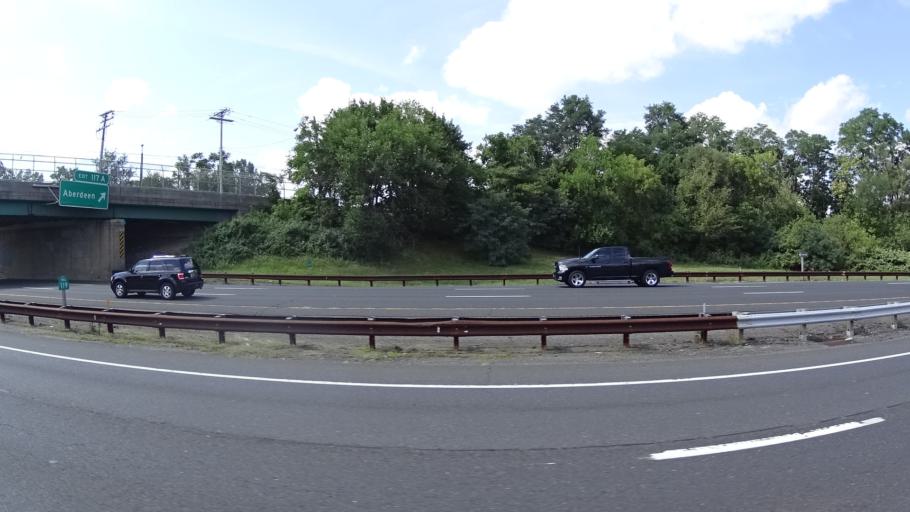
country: US
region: New Jersey
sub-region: Monmouth County
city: Matawan
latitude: 40.4236
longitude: -74.2180
